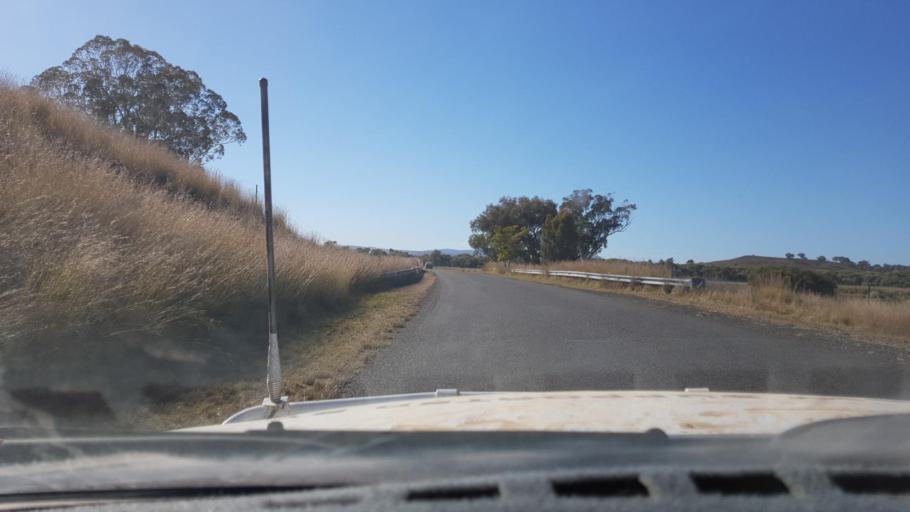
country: AU
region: New South Wales
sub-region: Narrabri
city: Blair Athol
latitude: -30.6766
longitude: 150.4253
